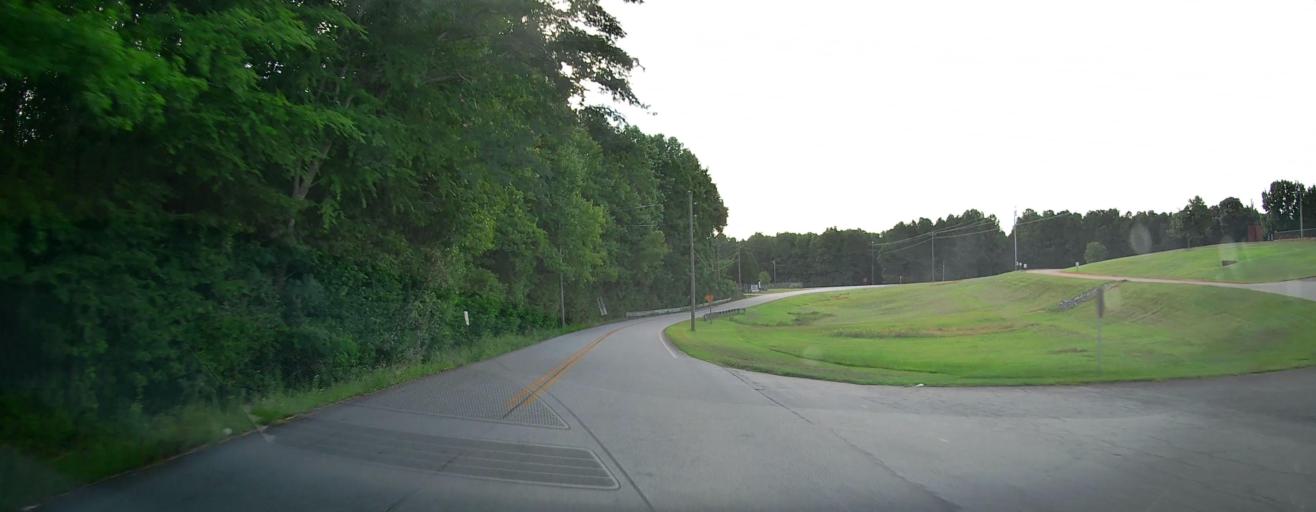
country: US
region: Georgia
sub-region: Monroe County
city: Forsyth
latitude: 33.0208
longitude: -83.9567
